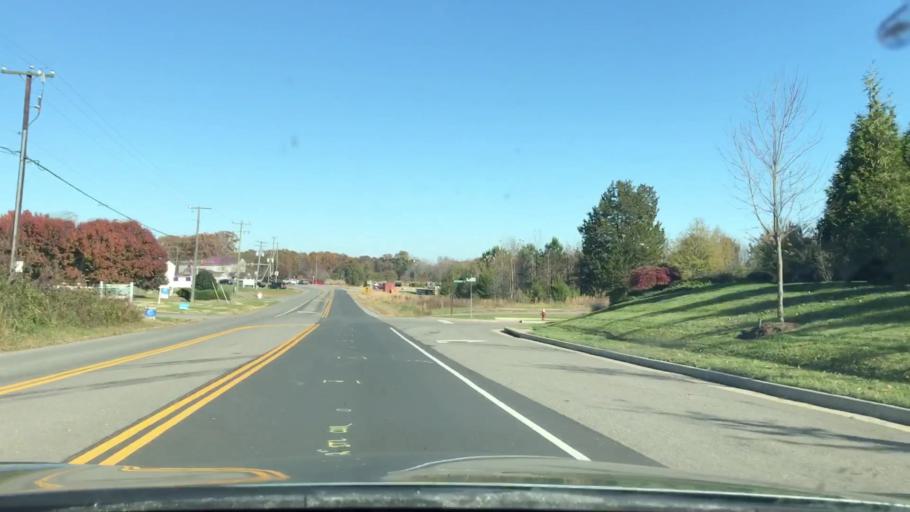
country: US
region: Virginia
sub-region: Henrico County
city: Short Pump
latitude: 37.6695
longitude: -77.6904
